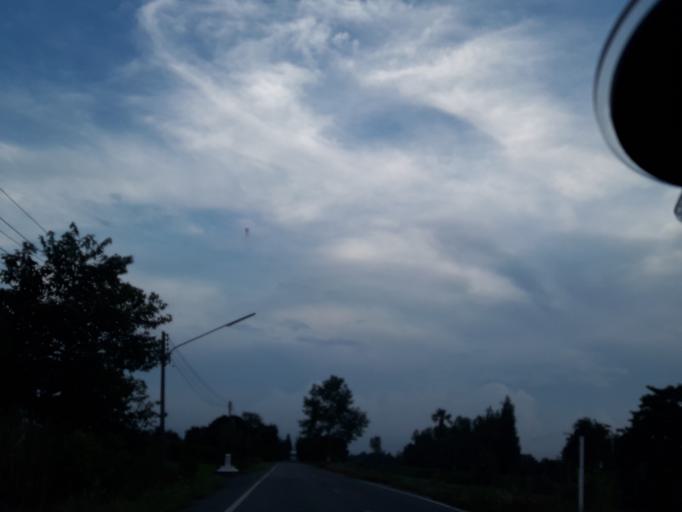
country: TH
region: Pathum Thani
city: Nong Suea
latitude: 14.1777
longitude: 100.8689
